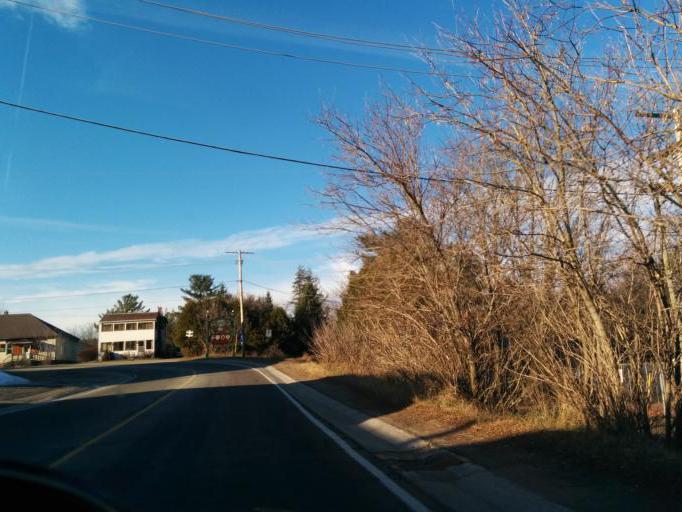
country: CA
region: Ontario
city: Bancroft
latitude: 45.0454
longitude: -78.5051
